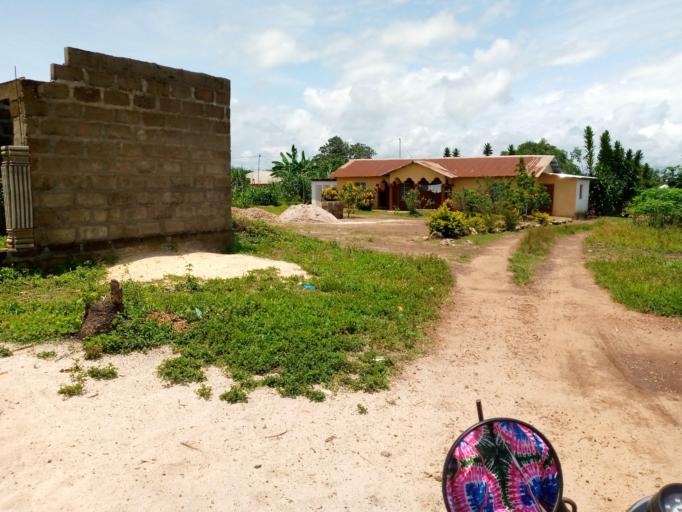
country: SL
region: Northern Province
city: Magburaka
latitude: 8.7242
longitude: -11.9266
